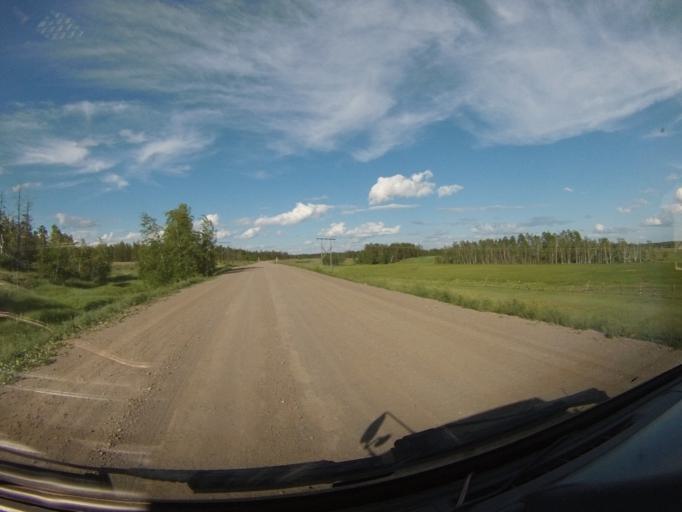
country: RU
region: Sakha
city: Ytyk-Kyuyel'
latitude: 62.2199
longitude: 133.2688
